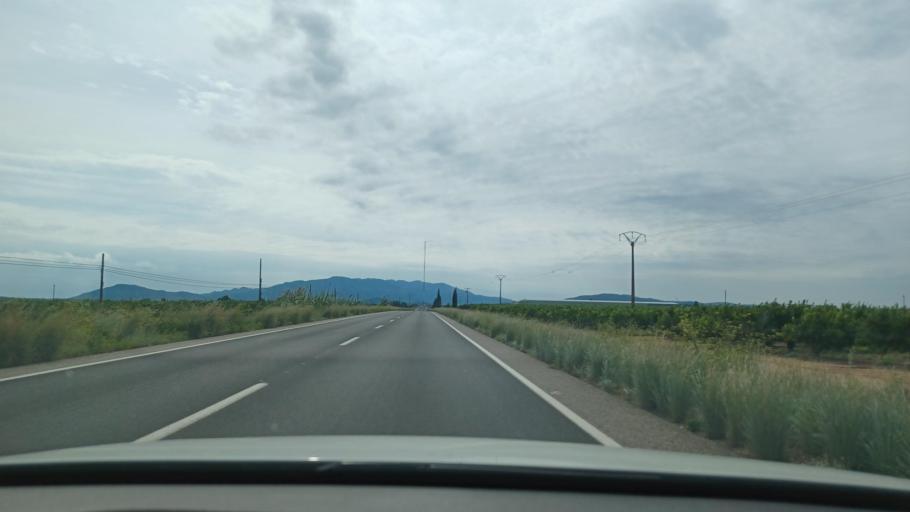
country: ES
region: Catalonia
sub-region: Provincia de Tarragona
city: Santa Barbara
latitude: 40.7465
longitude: 0.5032
